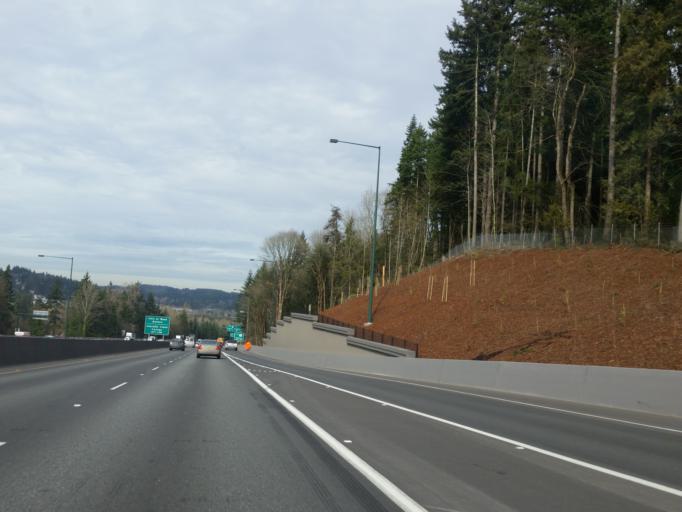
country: US
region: Washington
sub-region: King County
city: Kingsgate
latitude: 47.7487
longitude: -122.1865
